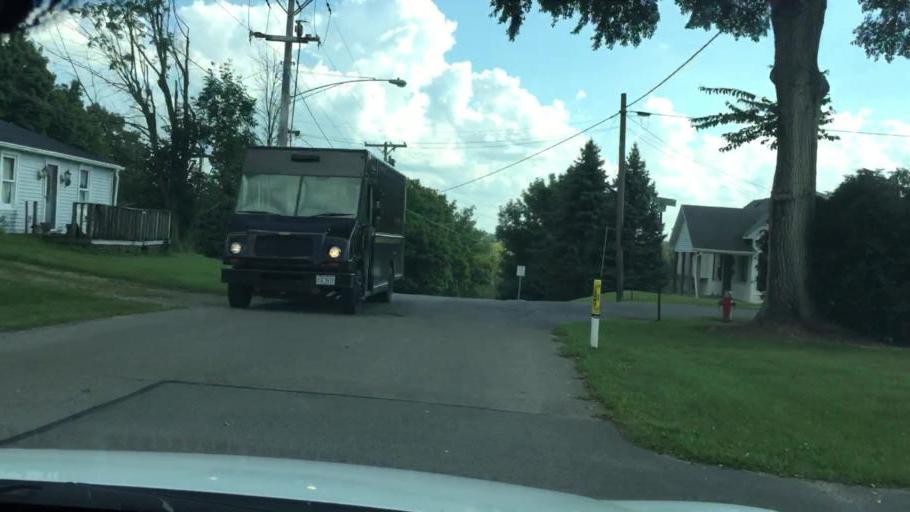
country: US
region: Ohio
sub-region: Champaign County
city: Mechanicsburg
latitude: 40.0742
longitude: -83.5634
